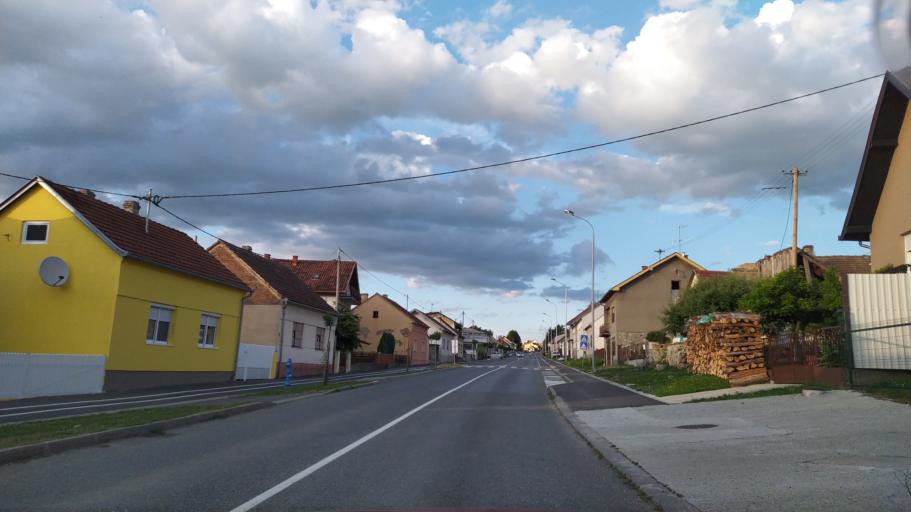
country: HR
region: Osjecko-Baranjska
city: Nasice
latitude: 45.4867
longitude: 18.0793
